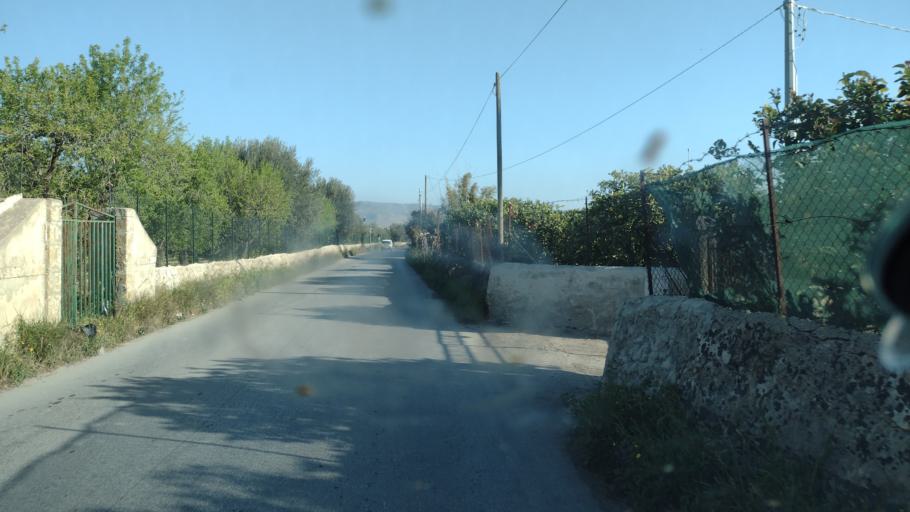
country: IT
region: Sicily
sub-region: Provincia di Siracusa
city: Avola
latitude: 36.8852
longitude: 15.1311
